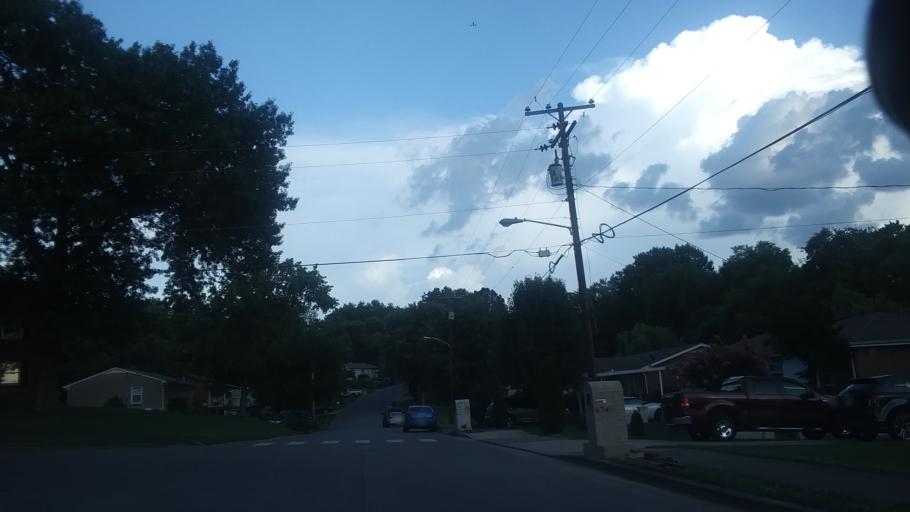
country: US
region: Tennessee
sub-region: Rutherford County
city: La Vergne
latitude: 36.0658
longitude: -86.6677
